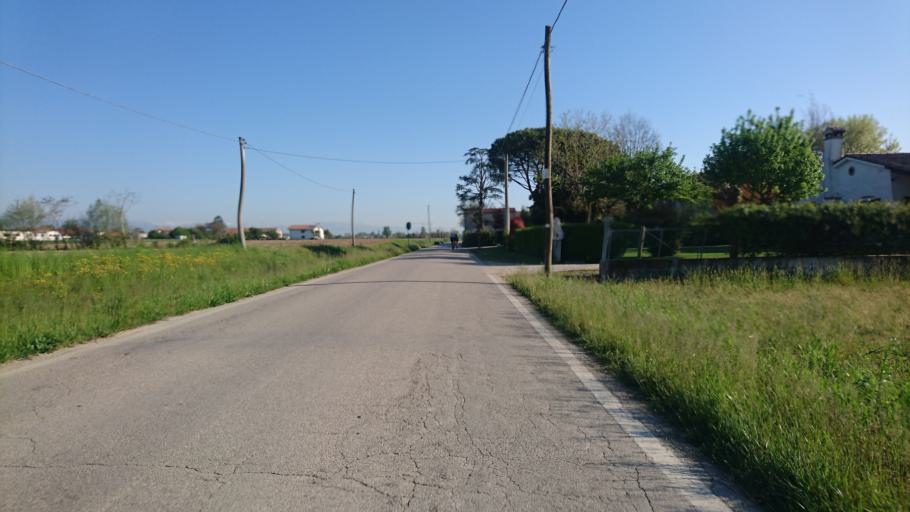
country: IT
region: Veneto
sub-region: Provincia di Venezia
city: Sant'Angelo
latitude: 45.5259
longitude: 12.0004
